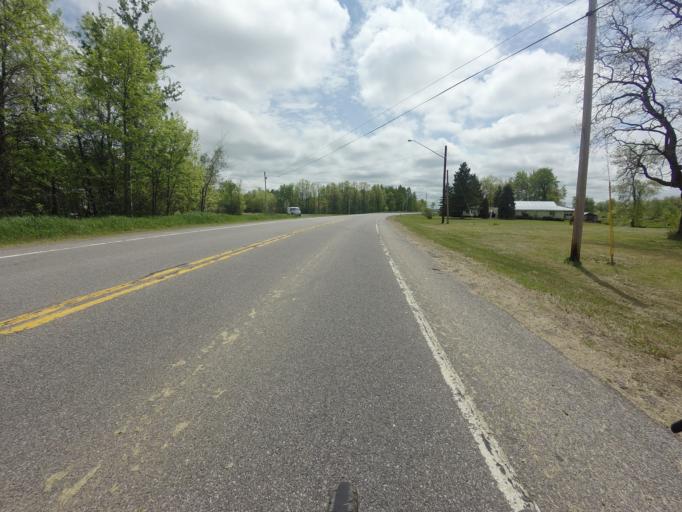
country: CA
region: Ontario
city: Cornwall
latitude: 44.9615
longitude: -74.6664
